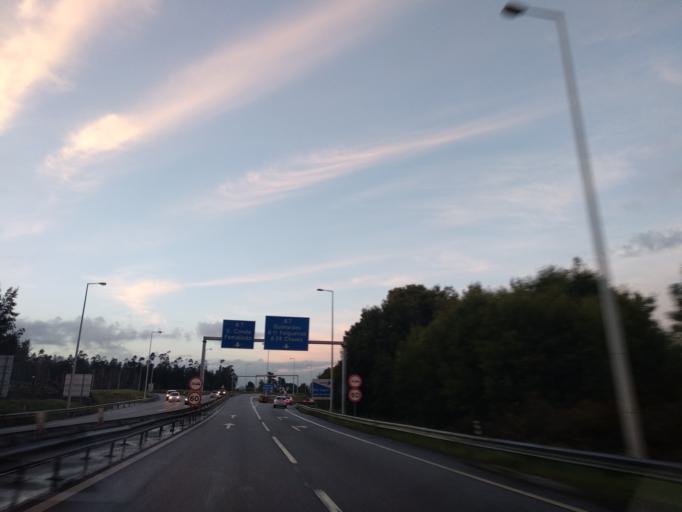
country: PT
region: Braga
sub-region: Vila Nova de Famalicao
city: Vila Nova de Famalicao
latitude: 41.3800
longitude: -8.5026
